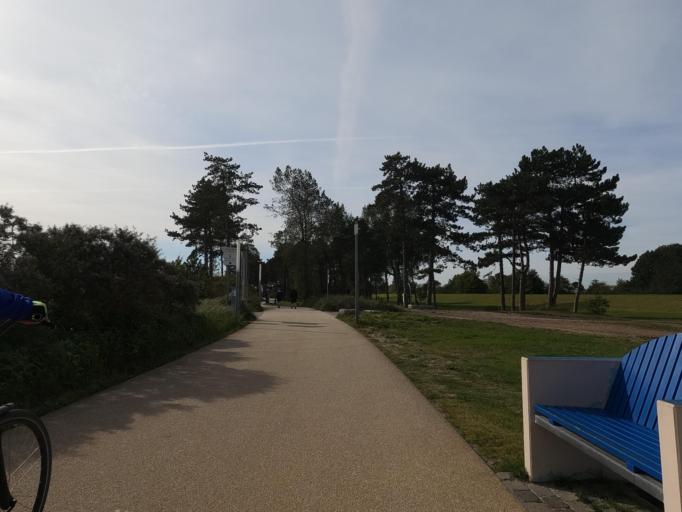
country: DE
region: Schleswig-Holstein
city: Kellenhusen
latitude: 54.1845
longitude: 11.0582
